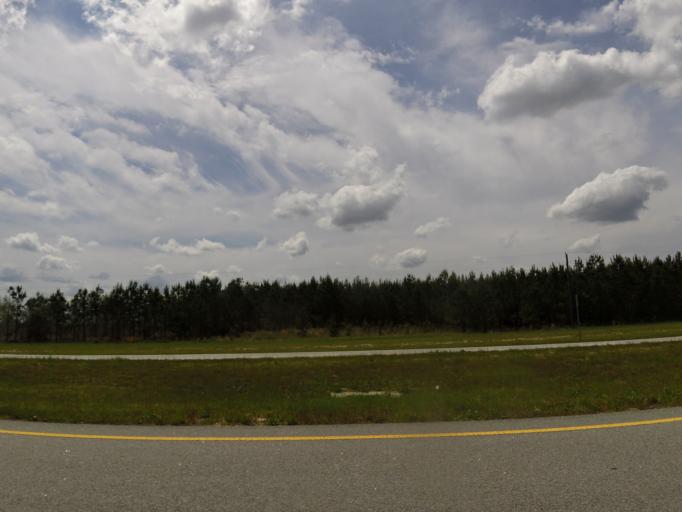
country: US
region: Georgia
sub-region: Jefferson County
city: Wadley
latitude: 32.7312
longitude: -82.3949
